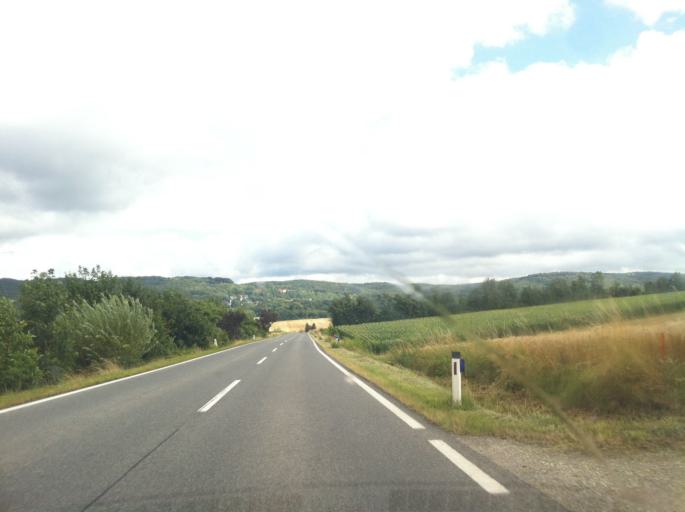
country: AT
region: Lower Austria
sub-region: Politischer Bezirk Tulln
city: Tulbing
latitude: 48.2684
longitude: 16.0737
